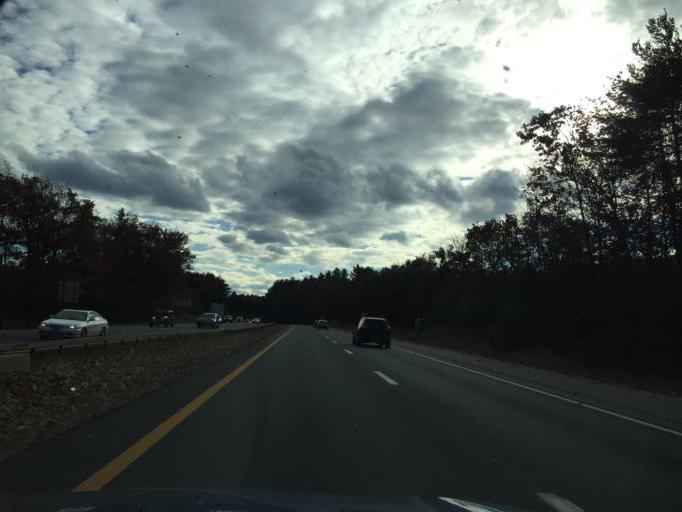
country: US
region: New Hampshire
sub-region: Hillsborough County
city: Litchfield
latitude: 42.8102
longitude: -71.4986
